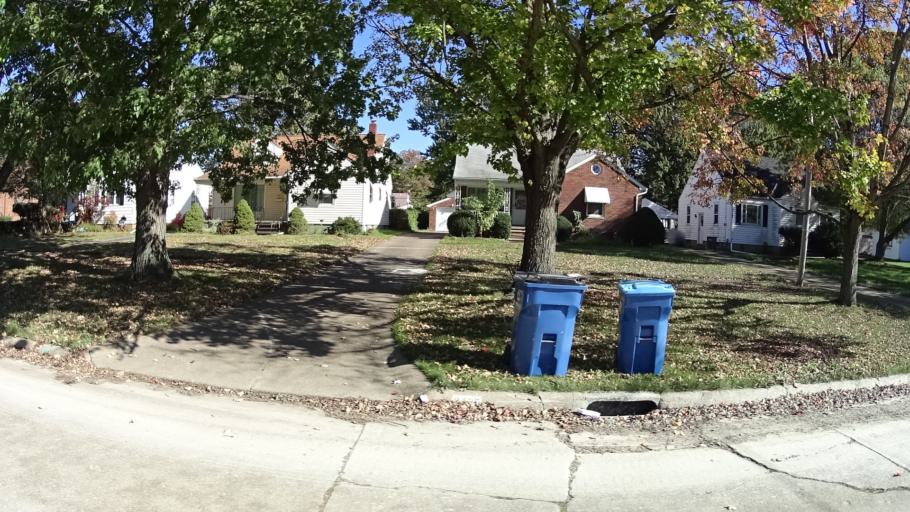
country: US
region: Ohio
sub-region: Lorain County
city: Lorain
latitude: 41.4383
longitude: -82.1715
